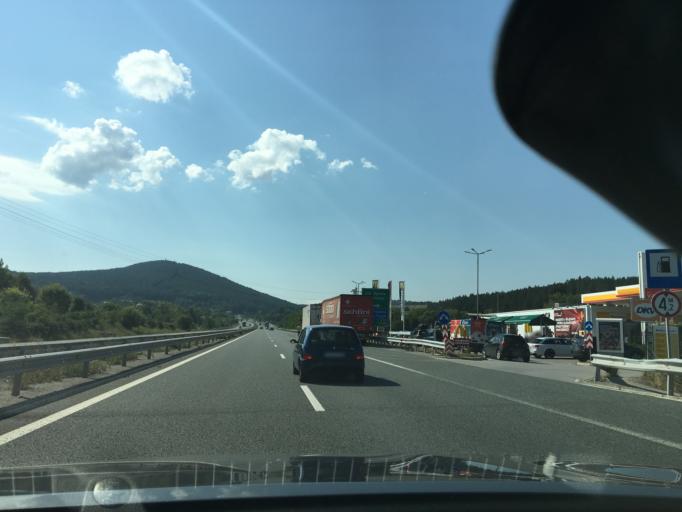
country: BG
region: Pernik
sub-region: Obshtina Pernik
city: Pernik
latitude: 42.5411
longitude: 23.1292
